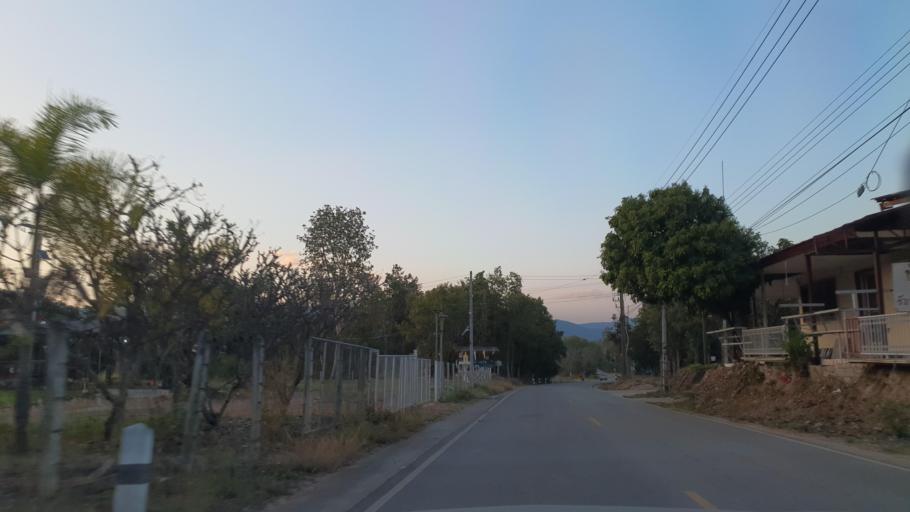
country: TH
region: Chiang Mai
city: Mae Wang
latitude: 18.6261
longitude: 98.8066
